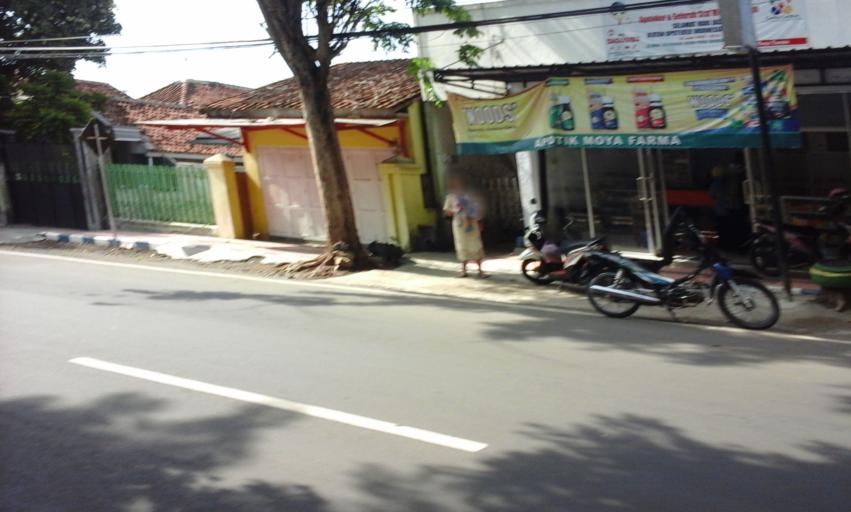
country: ID
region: East Java
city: Cungking
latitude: -8.2140
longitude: 114.3524
